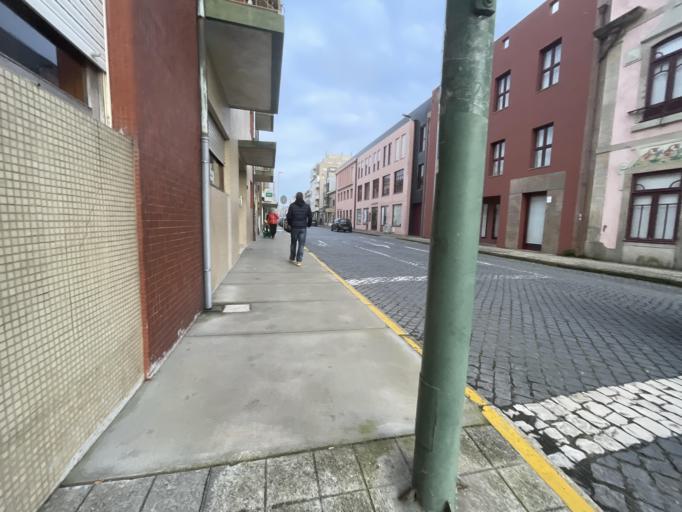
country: PT
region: Porto
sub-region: Vila do Conde
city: Vila do Conde
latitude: 41.3531
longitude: -8.7486
